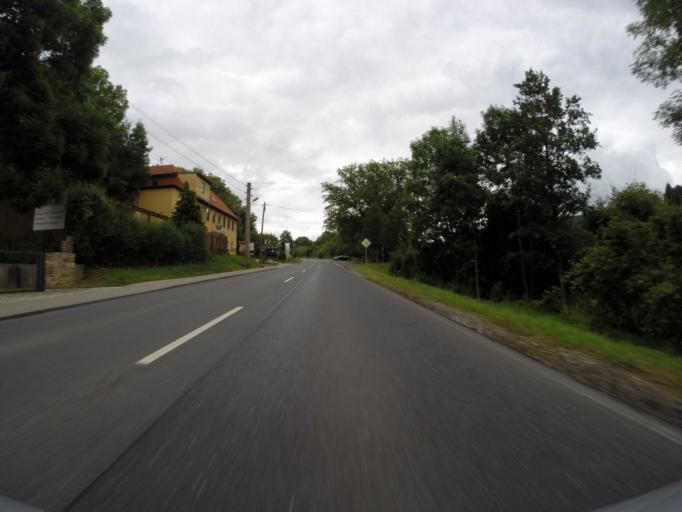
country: DE
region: Thuringia
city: Grosslobichau
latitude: 50.9321
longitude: 11.6607
